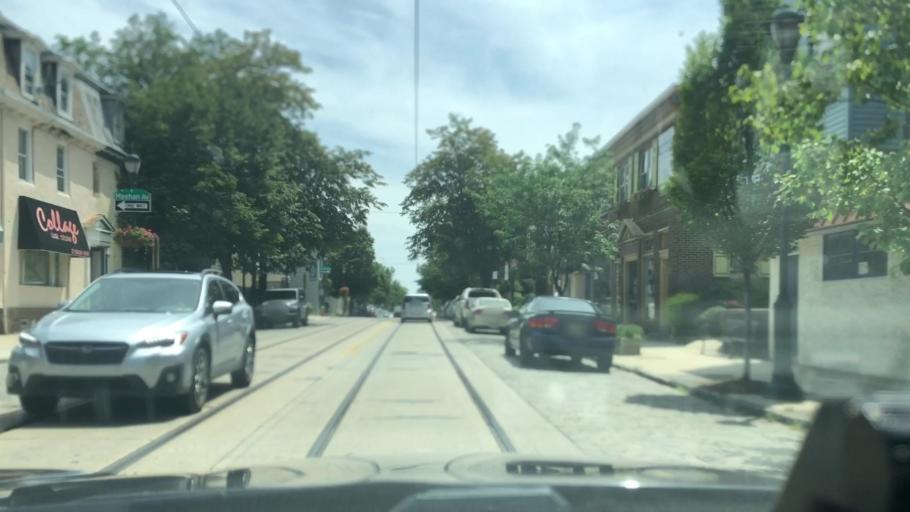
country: US
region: Pennsylvania
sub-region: Montgomery County
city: Wyndmoor
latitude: 40.0547
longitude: -75.1869
